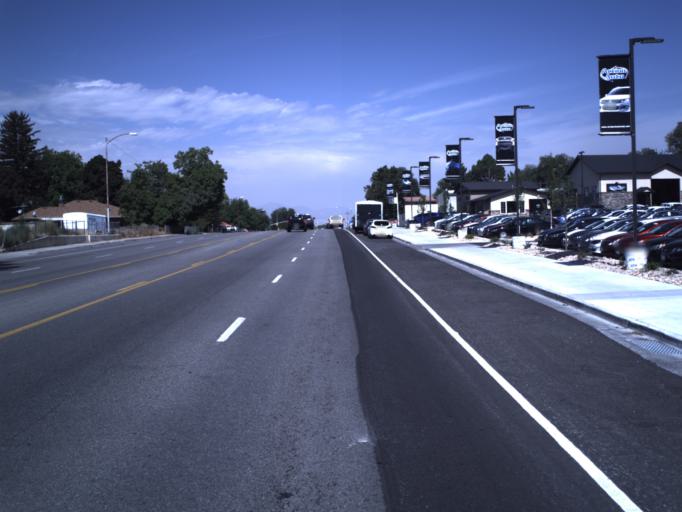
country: US
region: Utah
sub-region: Utah County
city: Lehi
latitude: 40.3992
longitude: -111.8509
